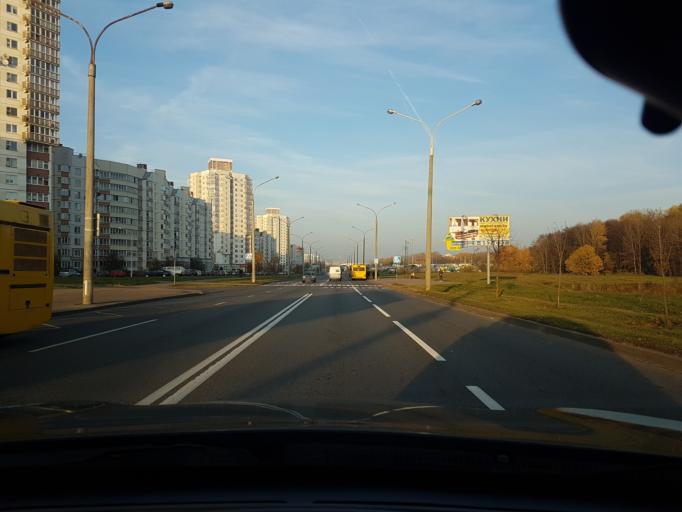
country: BY
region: Minsk
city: Shchomyslitsa
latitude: 53.8433
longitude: 27.4823
